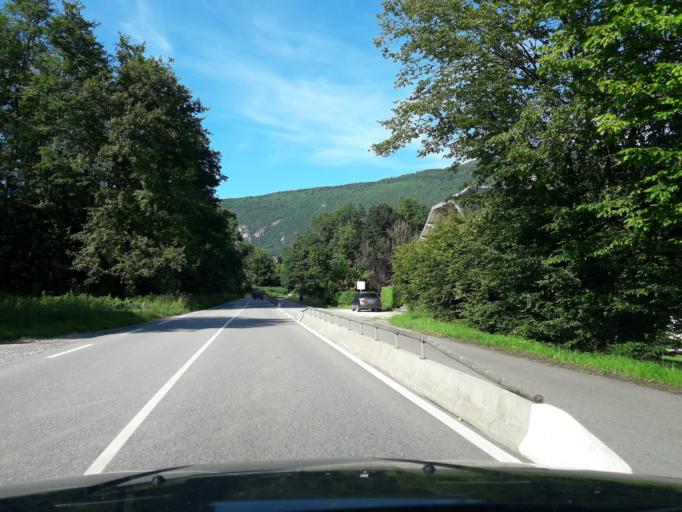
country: FR
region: Rhone-Alpes
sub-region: Departement de la Savoie
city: Novalaise
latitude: 45.5590
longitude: 5.7900
